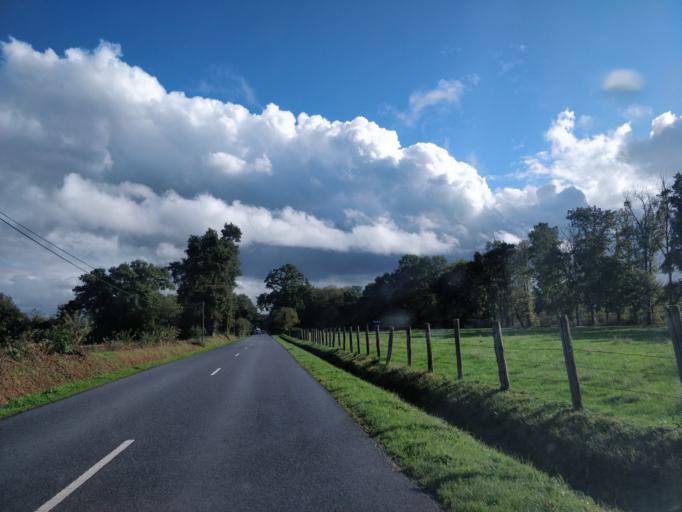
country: FR
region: Brittany
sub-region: Departement d'Ille-et-Vilaine
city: La Bouexiere
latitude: 48.1595
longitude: -1.4153
